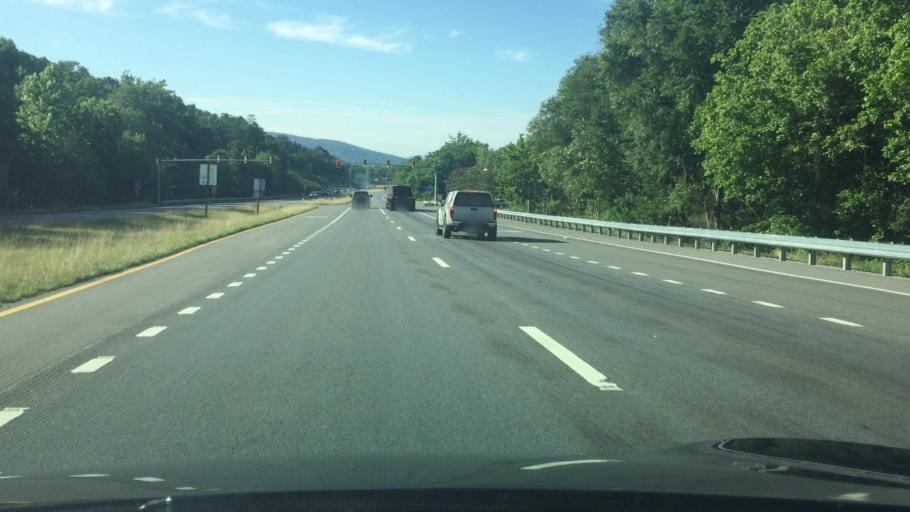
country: US
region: Virginia
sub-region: Botetourt County
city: Cloverdale
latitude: 37.3536
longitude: -79.8846
